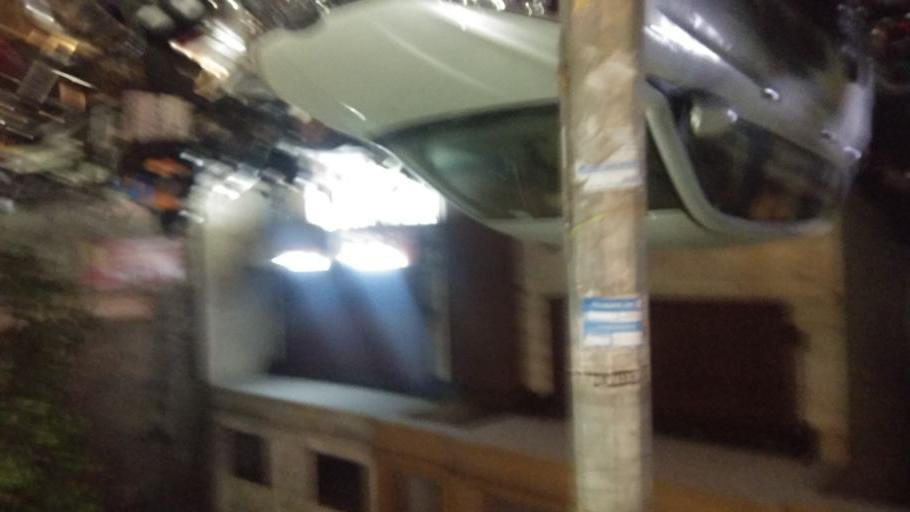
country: IN
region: Maharashtra
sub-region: Pune Division
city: Pune
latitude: 18.5186
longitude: 73.8567
